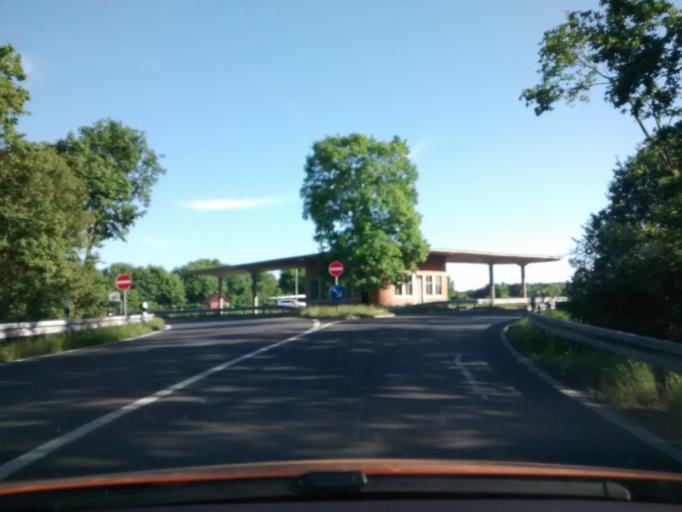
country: DE
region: Brandenburg
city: Langewahl
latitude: 52.3355
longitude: 14.0776
